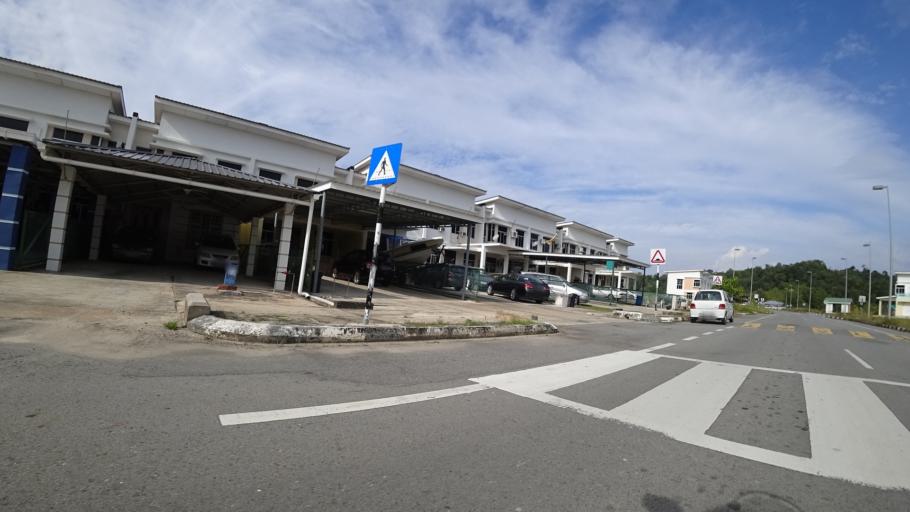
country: BN
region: Brunei and Muara
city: Bandar Seri Begawan
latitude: 4.8868
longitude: 114.7976
